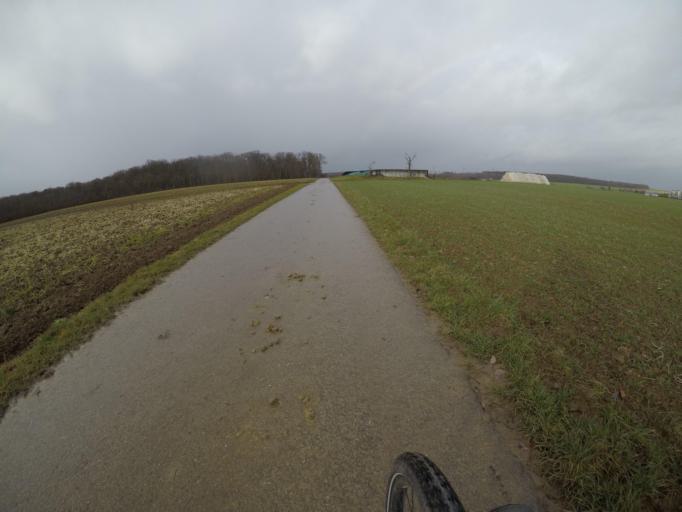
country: DE
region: Baden-Wuerttemberg
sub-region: Regierungsbezirk Stuttgart
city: Hemmingen
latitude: 48.8574
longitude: 9.0190
